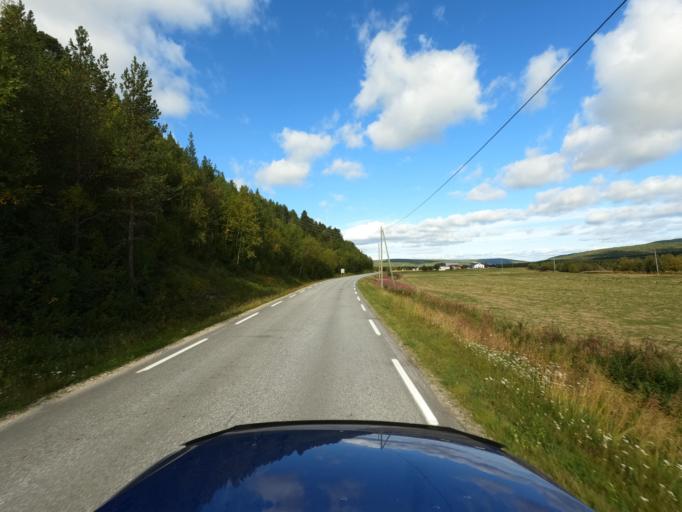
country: NO
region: Finnmark Fylke
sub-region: Karasjok
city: Karasjohka
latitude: 69.4077
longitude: 25.8072
